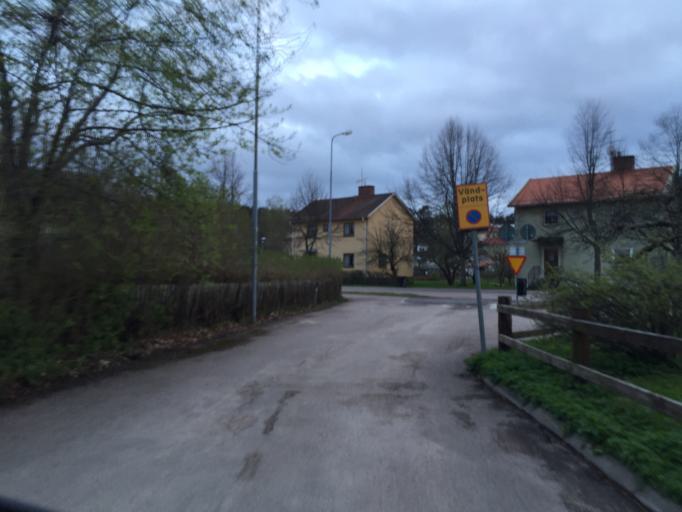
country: SE
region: Dalarna
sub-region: Ludvika Kommun
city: Ludvika
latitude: 60.1454
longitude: 15.1939
